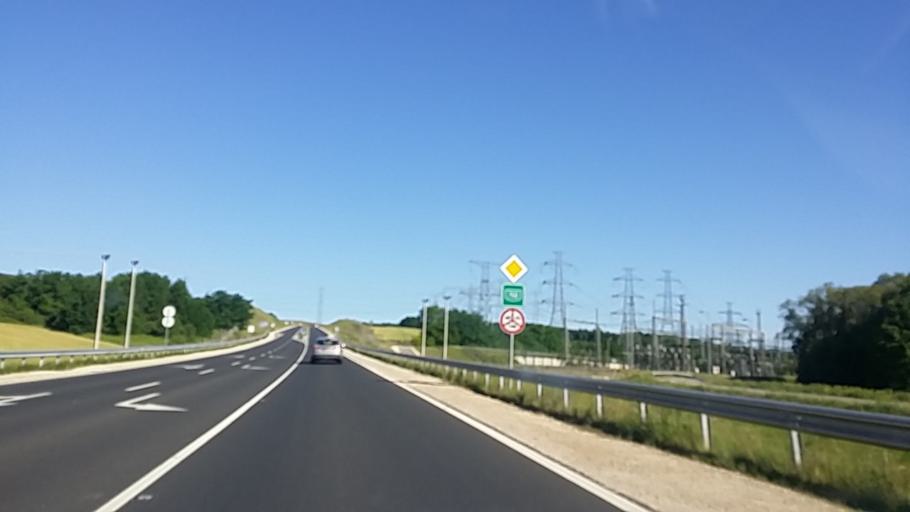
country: HU
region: Zala
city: Heviz
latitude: 46.7885
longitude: 17.1716
